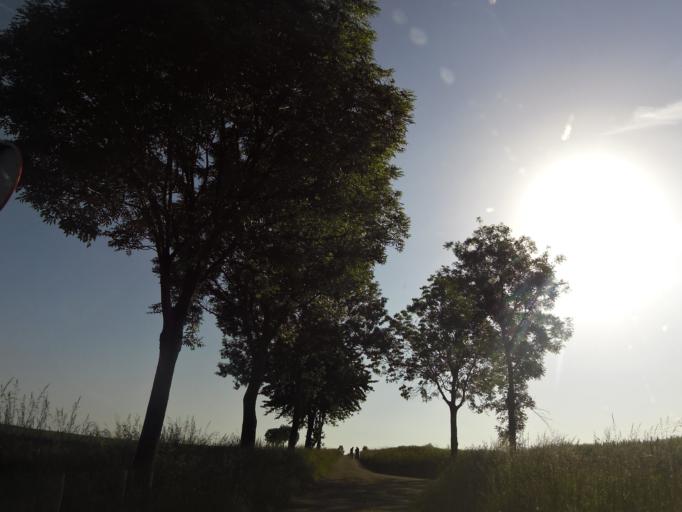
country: NL
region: Limburg
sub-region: Valkenburg aan de Geul
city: Schin op Geul
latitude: 50.8499
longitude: 5.8895
